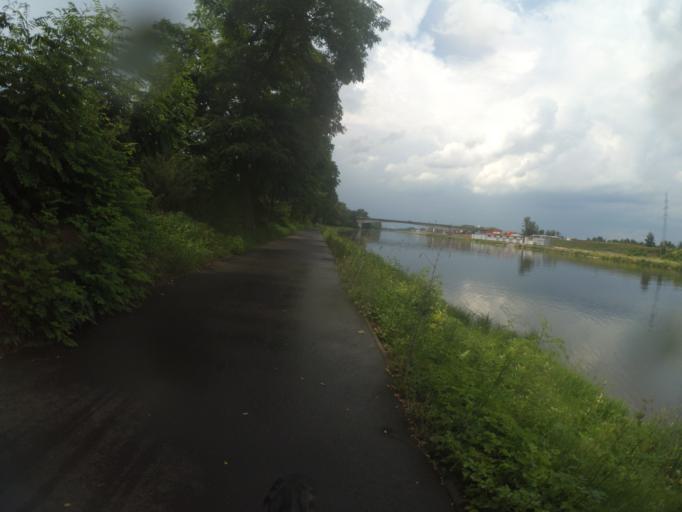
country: CZ
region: Central Bohemia
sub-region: Okres Melnik
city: Melnik
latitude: 50.3543
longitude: 14.4643
